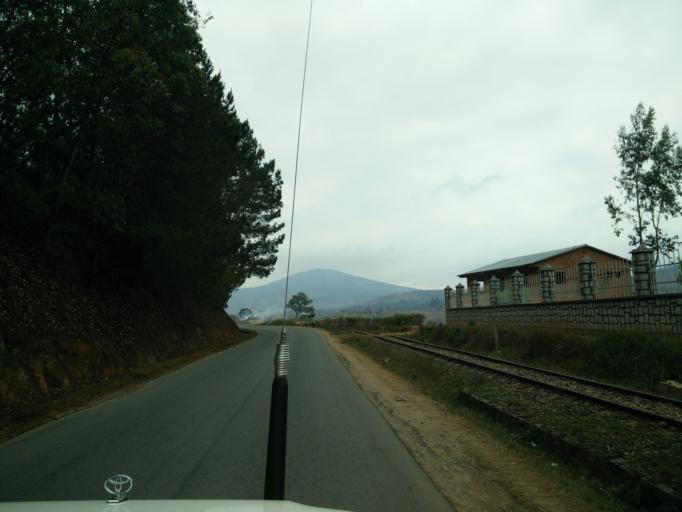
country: MG
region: Upper Matsiatra
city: Fianarantsoa
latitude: -21.4311
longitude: 47.1344
